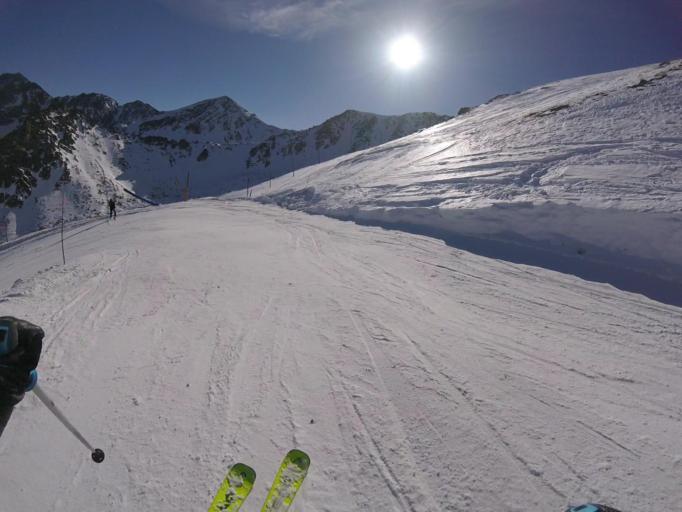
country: AD
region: Encamp
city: Pas de la Casa
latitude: 42.5262
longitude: 1.7256
